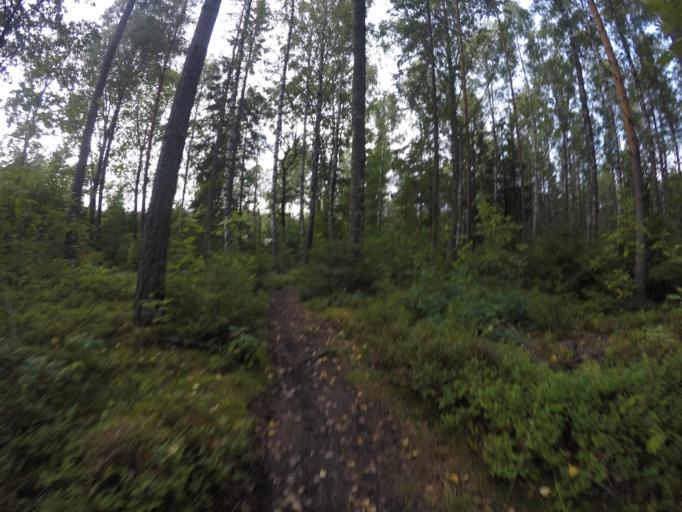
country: SE
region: Vaestmanland
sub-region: Vasteras
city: Vasteras
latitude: 59.6412
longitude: 16.5198
